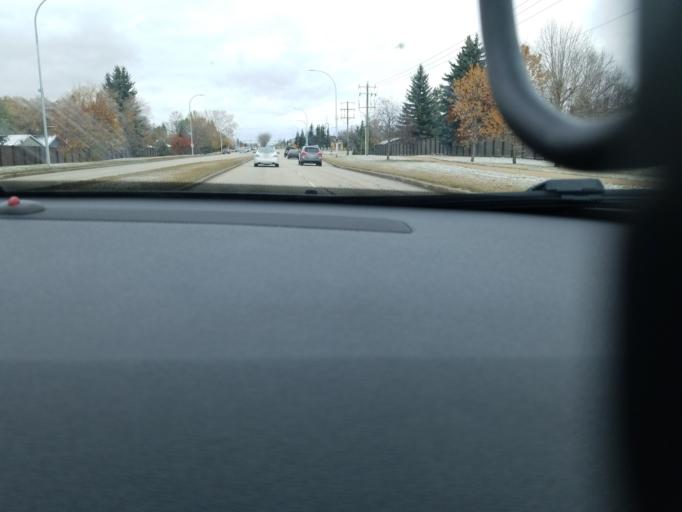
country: CA
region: Alberta
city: Sherwood Park
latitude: 53.5370
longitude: -113.2956
